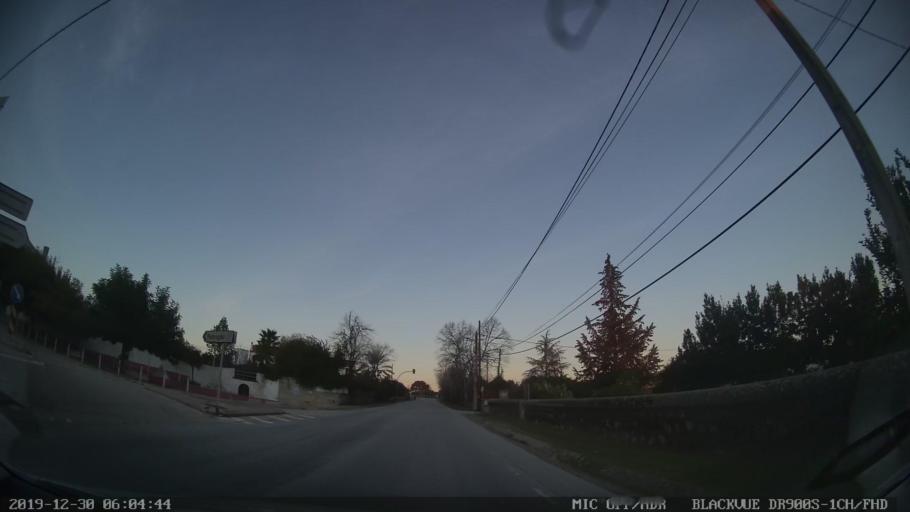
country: PT
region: Castelo Branco
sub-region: Penamacor
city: Penamacor
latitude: 40.0861
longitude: -7.2367
